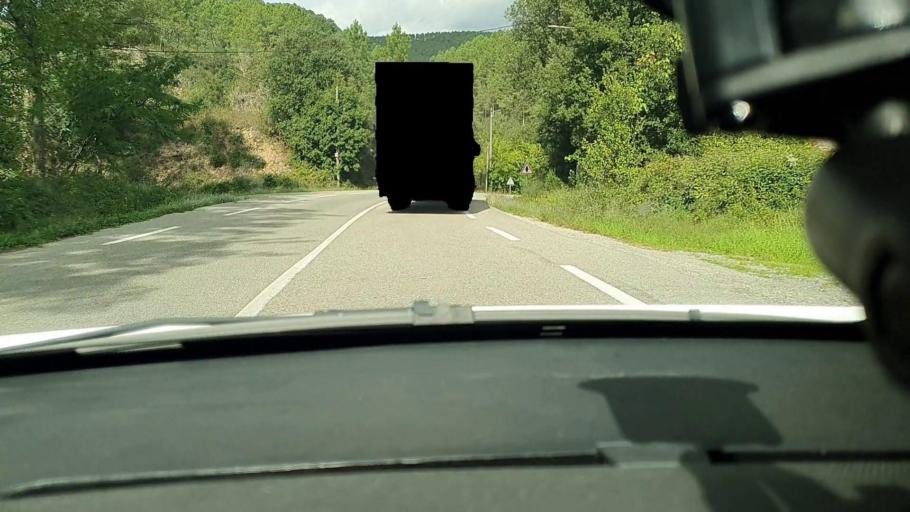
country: FR
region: Languedoc-Roussillon
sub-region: Departement du Gard
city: Besseges
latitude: 44.2561
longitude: 4.0669
